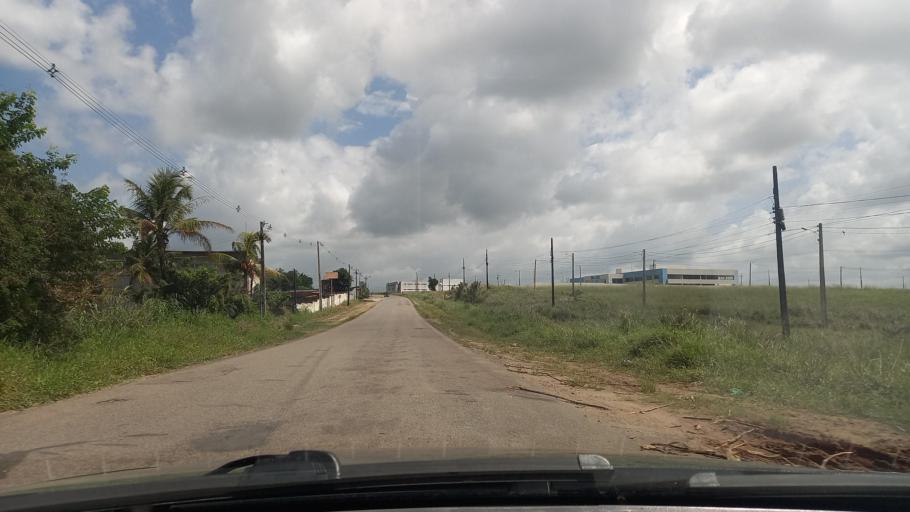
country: BR
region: Pernambuco
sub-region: Goiana
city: Goiana
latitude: -7.5587
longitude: -35.0228
